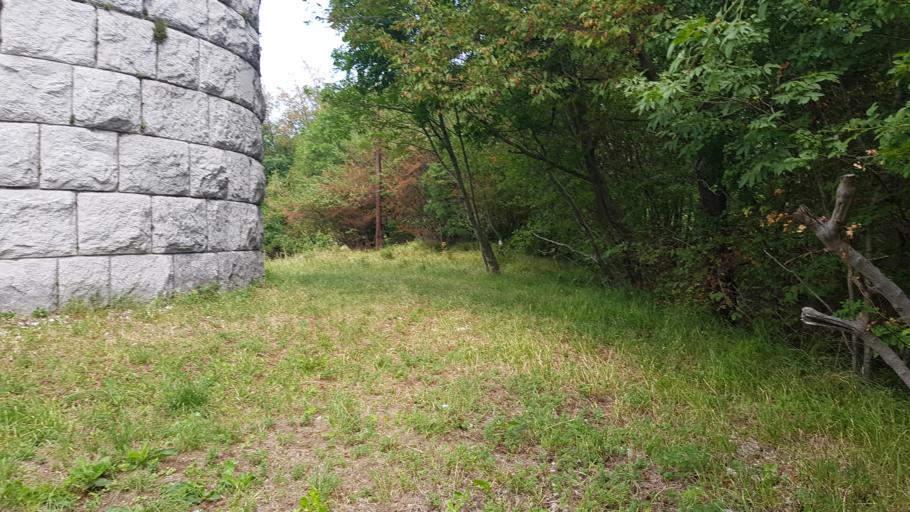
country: SI
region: Kanal
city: Deskle
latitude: 46.0144
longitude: 13.6364
